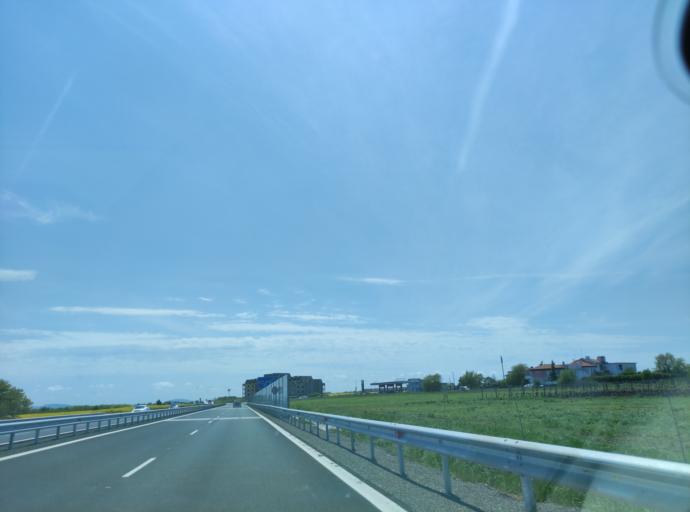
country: BG
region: Burgas
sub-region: Obshtina Pomorie
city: Pomorie
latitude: 42.5635
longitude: 27.5710
